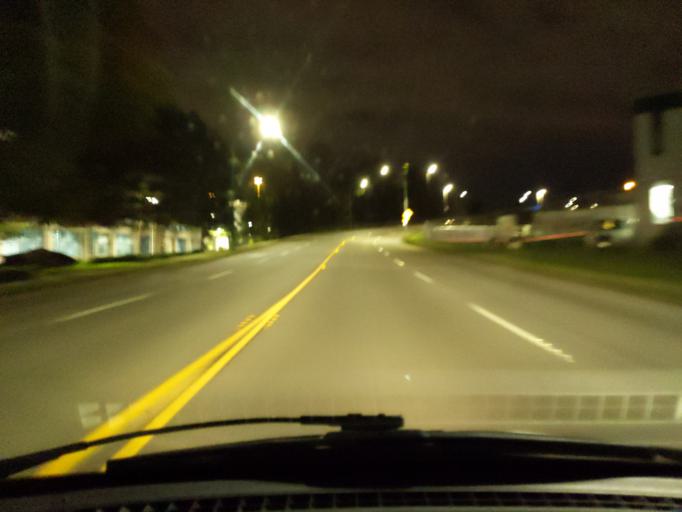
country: CA
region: British Columbia
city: Burnaby
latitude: 49.2597
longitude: -123.0131
